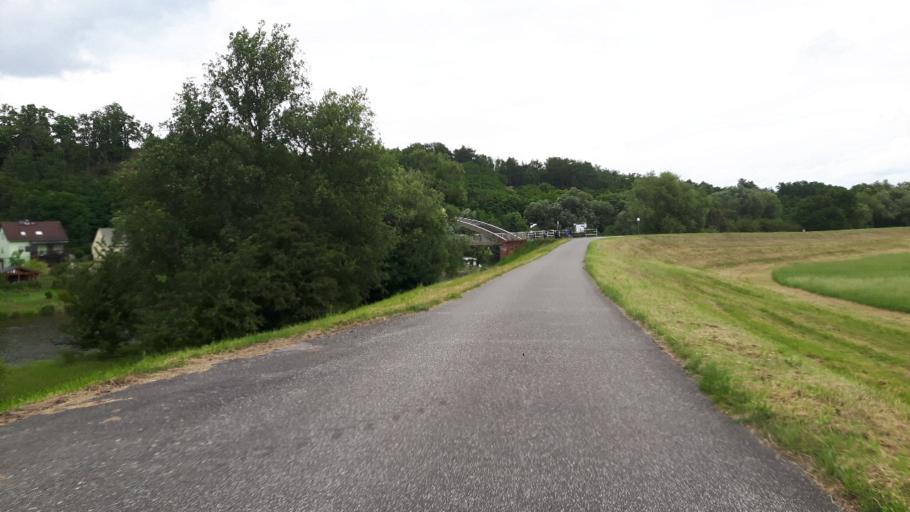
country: DE
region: Brandenburg
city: Schoneberg
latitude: 52.9912
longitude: 14.1752
